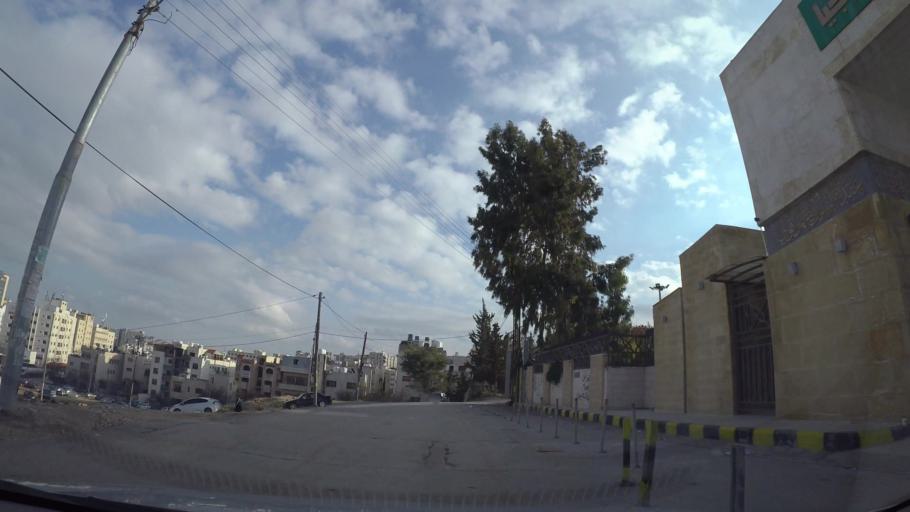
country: JO
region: Amman
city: Al Jubayhah
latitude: 32.0066
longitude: 35.8708
